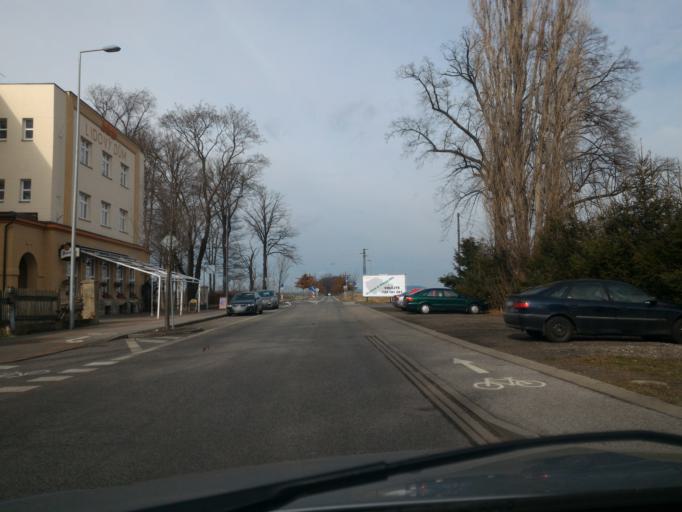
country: CZ
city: Hradek nad Nisou
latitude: 50.8583
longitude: 14.8392
